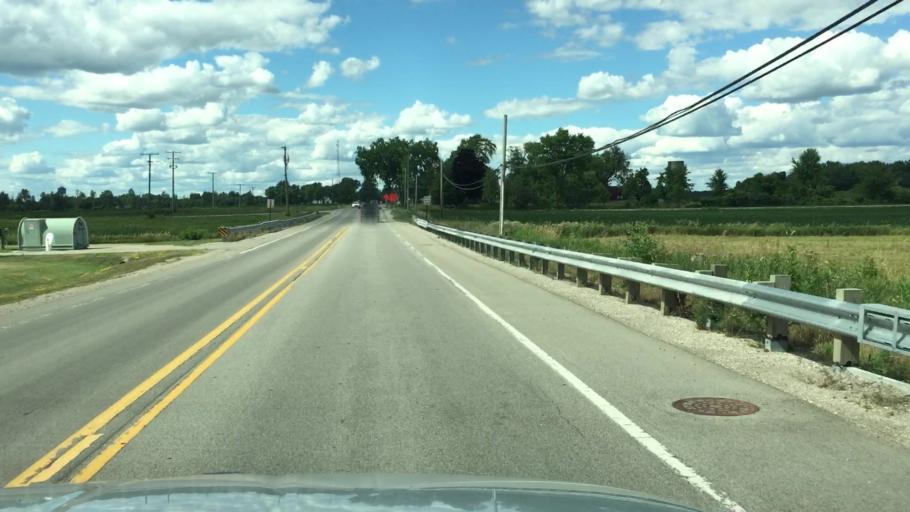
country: US
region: Michigan
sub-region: Saint Clair County
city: Capac
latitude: 42.9965
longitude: -82.9281
